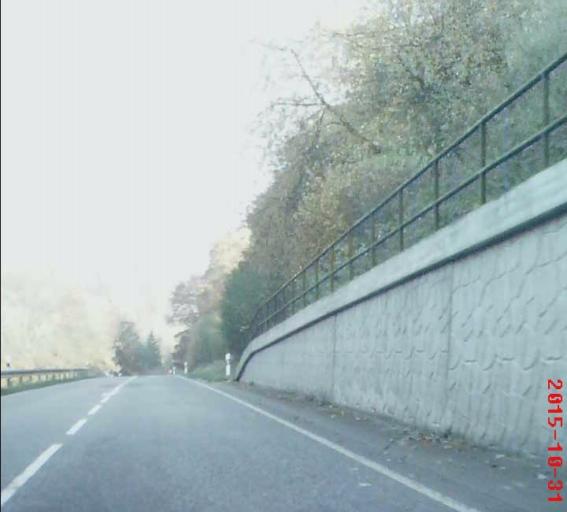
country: DE
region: Thuringia
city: Fretterode
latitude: 51.3047
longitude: 10.0245
